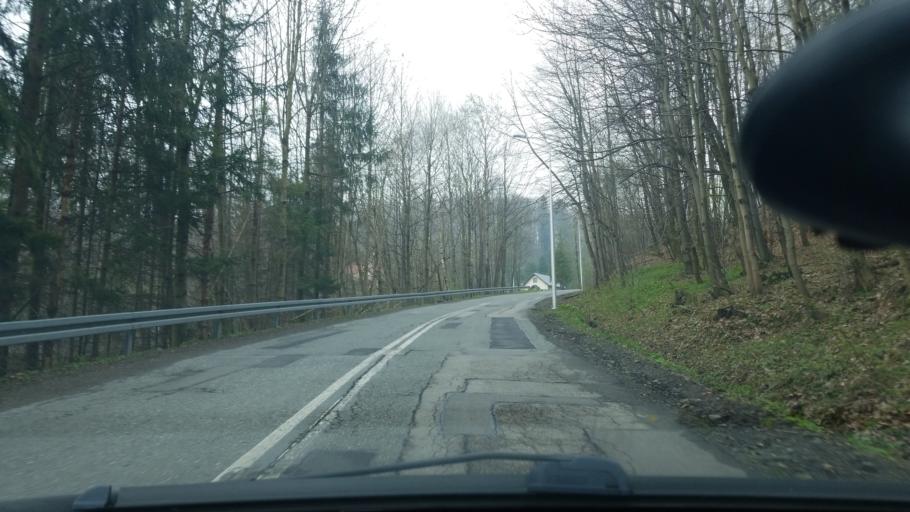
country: PL
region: Silesian Voivodeship
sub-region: Powiat cieszynski
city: Ustron
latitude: 49.7058
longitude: 18.8324
